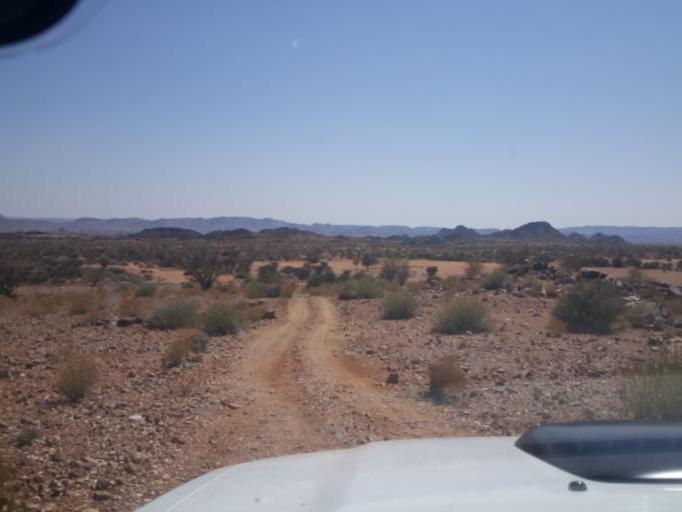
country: ZA
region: Northern Cape
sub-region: Siyanda District Municipality
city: Kakamas
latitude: -28.5888
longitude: 20.2550
